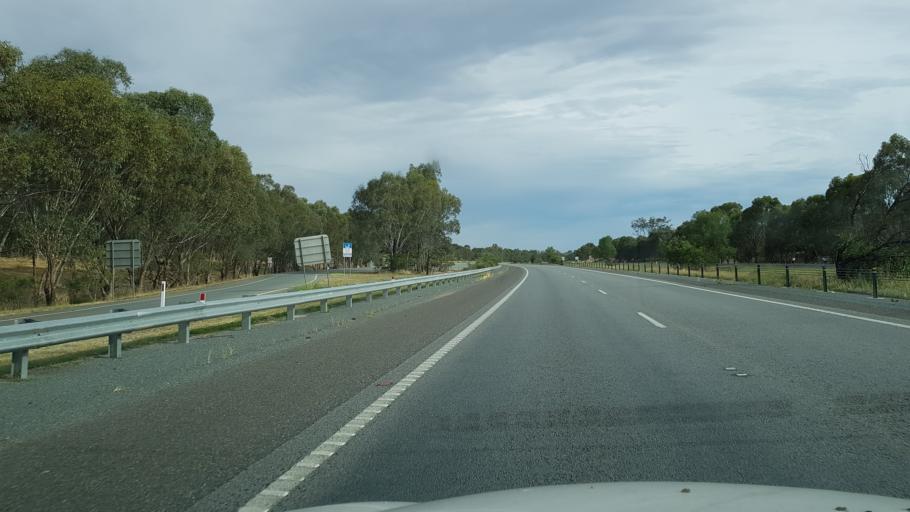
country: AU
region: Victoria
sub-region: Wangaratta
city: Wangaratta
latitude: -36.3324
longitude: 146.3753
